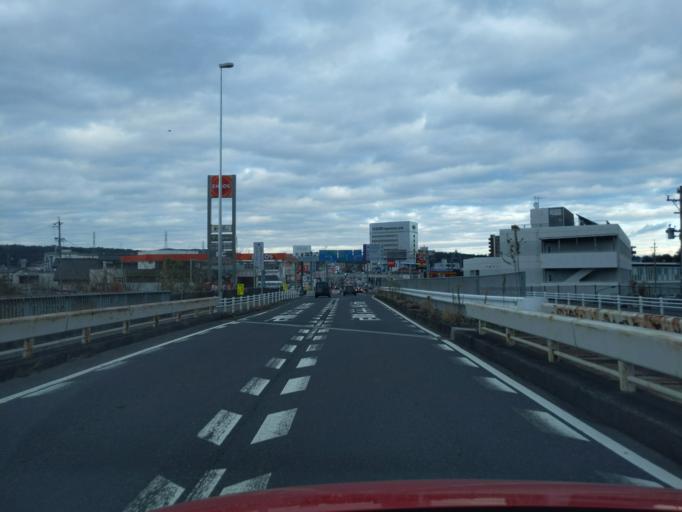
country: JP
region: Gifu
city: Tajimi
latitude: 35.3375
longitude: 137.1143
